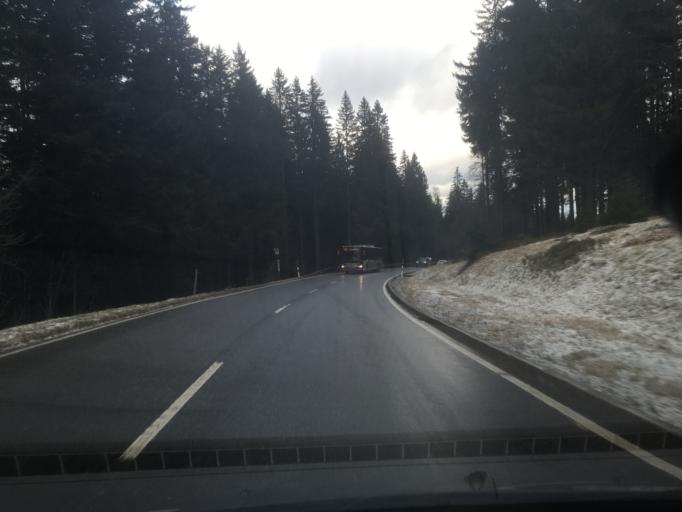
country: DE
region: Baden-Wuerttemberg
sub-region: Freiburg Region
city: Hinterzarten
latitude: 47.8612
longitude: 8.0680
